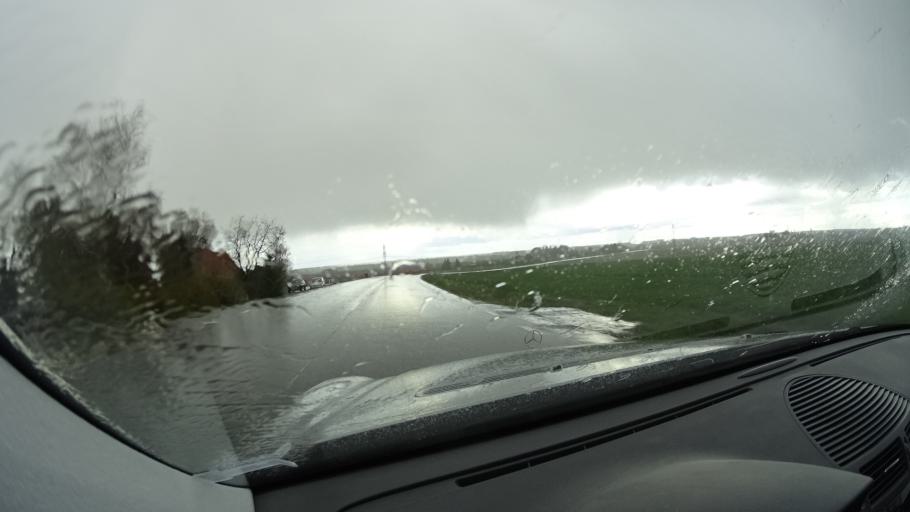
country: SE
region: Skane
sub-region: Lunds Kommun
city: Lund
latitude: 55.7659
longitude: 13.2225
